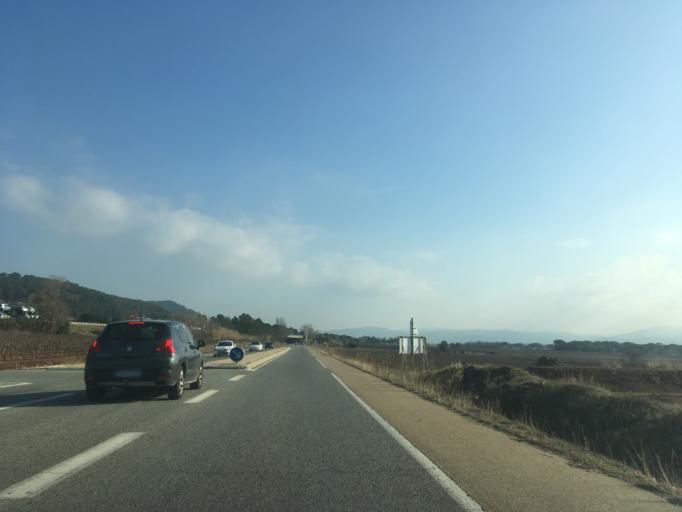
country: FR
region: Provence-Alpes-Cote d'Azur
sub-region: Departement du Var
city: Le Cannet-des-Maures
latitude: 43.4006
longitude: 6.3760
